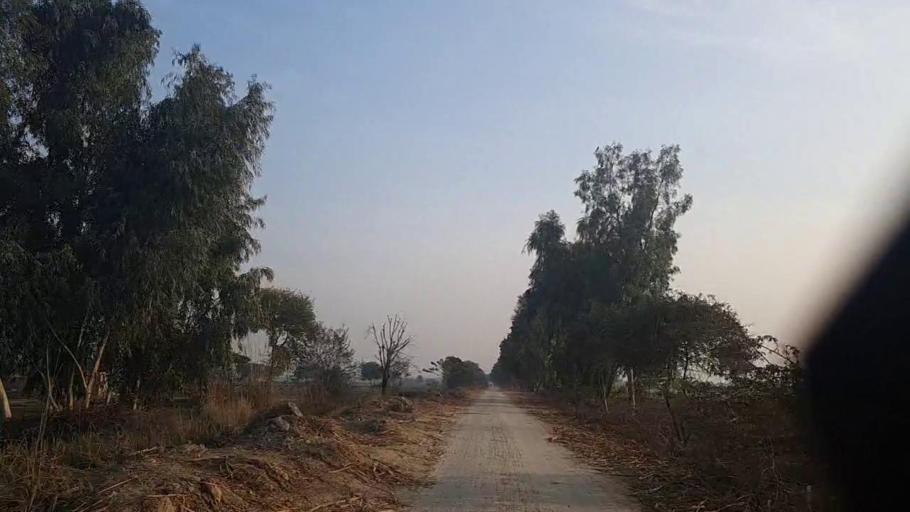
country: PK
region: Sindh
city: Sakrand
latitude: 26.1243
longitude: 68.2304
